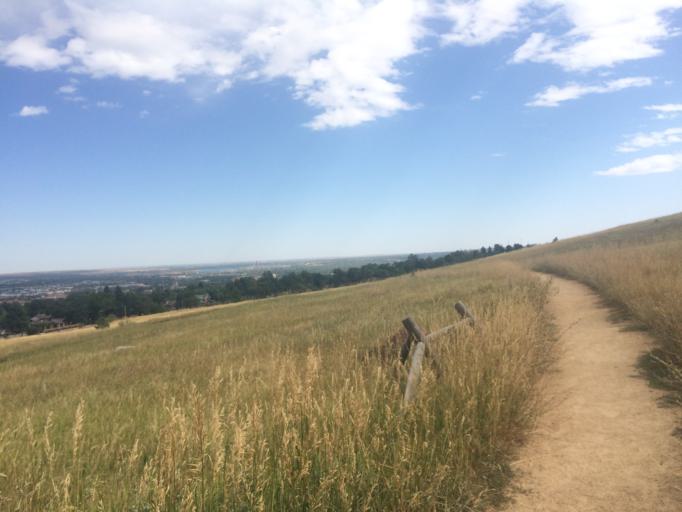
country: US
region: Colorado
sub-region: Boulder County
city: Boulder
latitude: 39.9985
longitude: -105.2878
